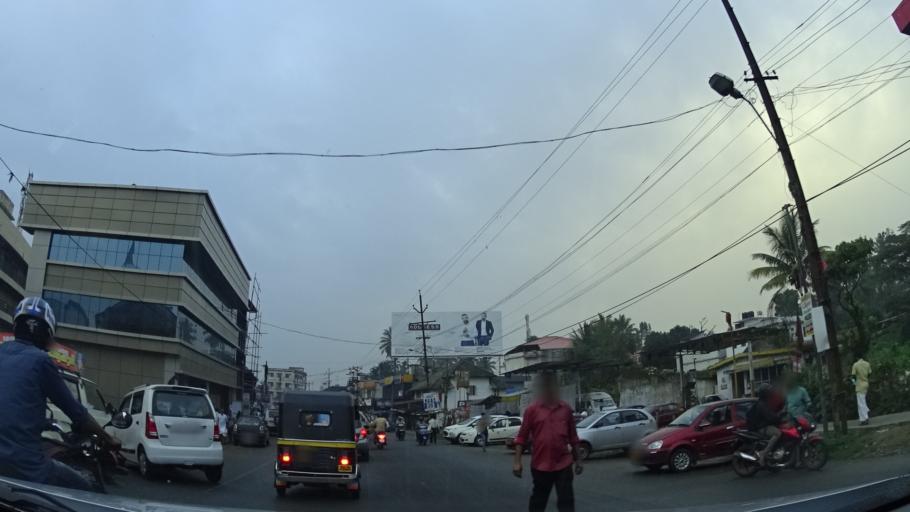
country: IN
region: Kerala
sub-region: Wayanad
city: Kalpetta
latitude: 11.6091
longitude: 76.0834
